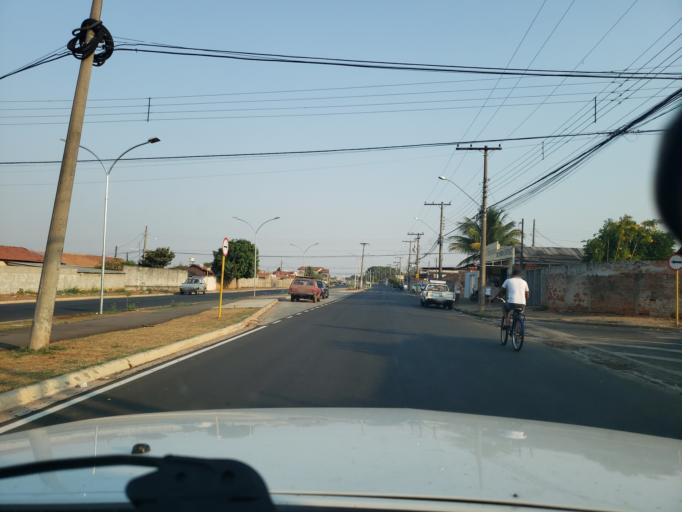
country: BR
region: Sao Paulo
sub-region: Moji-Guacu
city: Mogi-Gaucu
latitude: -22.3292
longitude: -46.9497
